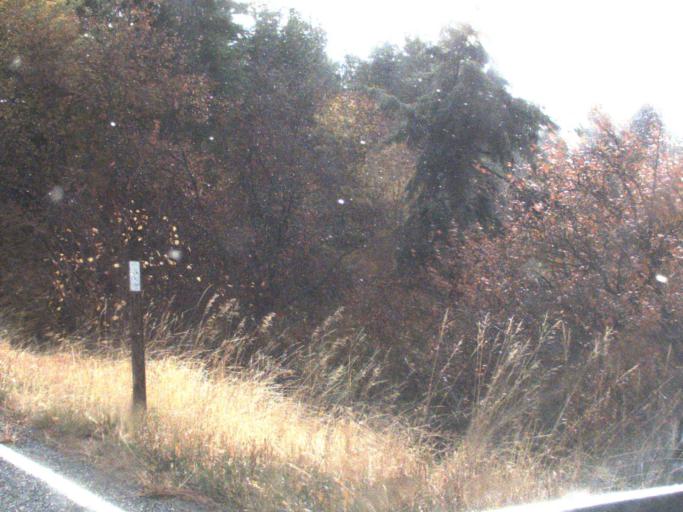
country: US
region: Washington
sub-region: Stevens County
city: Kettle Falls
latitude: 48.4247
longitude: -118.1697
